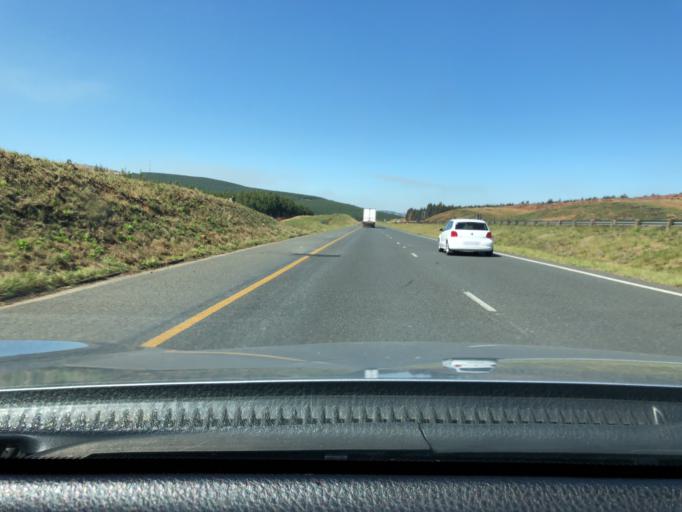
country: ZA
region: KwaZulu-Natal
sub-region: uMgungundlovu District Municipality
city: Howick
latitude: -29.3795
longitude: 30.1266
